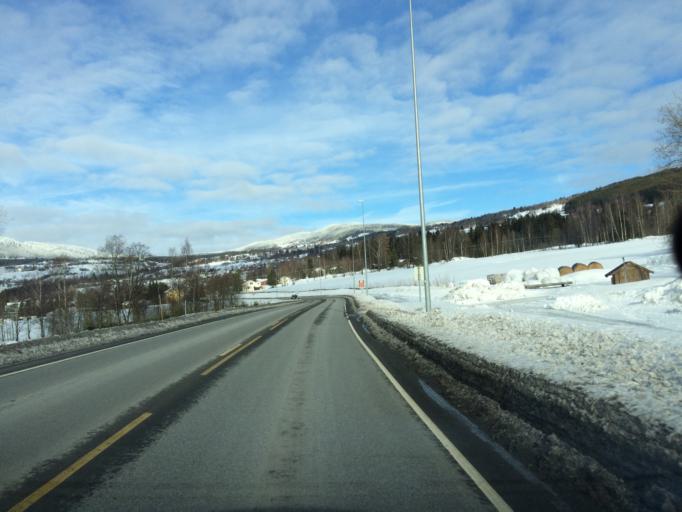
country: NO
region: Oppland
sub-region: Gausdal
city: Segalstad bru
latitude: 61.2082
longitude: 10.2982
